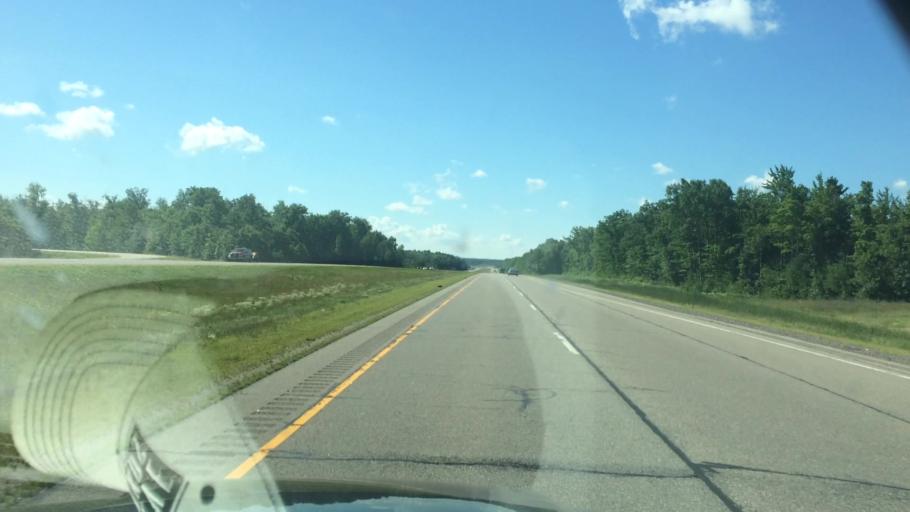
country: US
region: Wisconsin
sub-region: Portage County
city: Stevens Point
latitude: 44.5932
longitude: -89.6139
